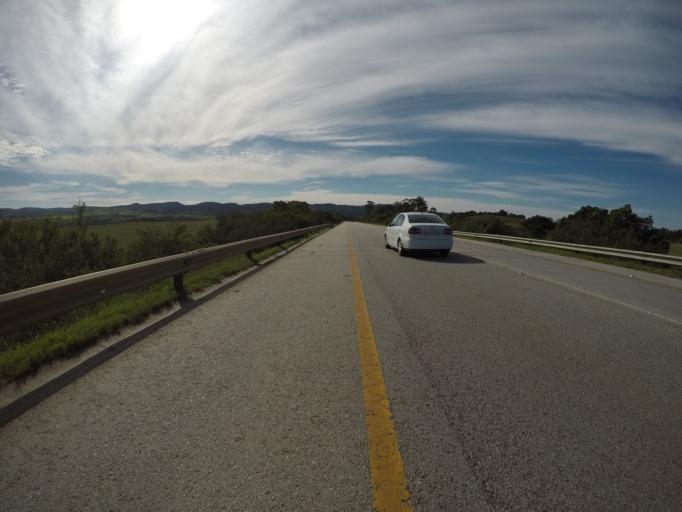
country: ZA
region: Eastern Cape
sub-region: Cacadu District Municipality
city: Jeffrey's Bay
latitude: -33.8944
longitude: 25.1283
